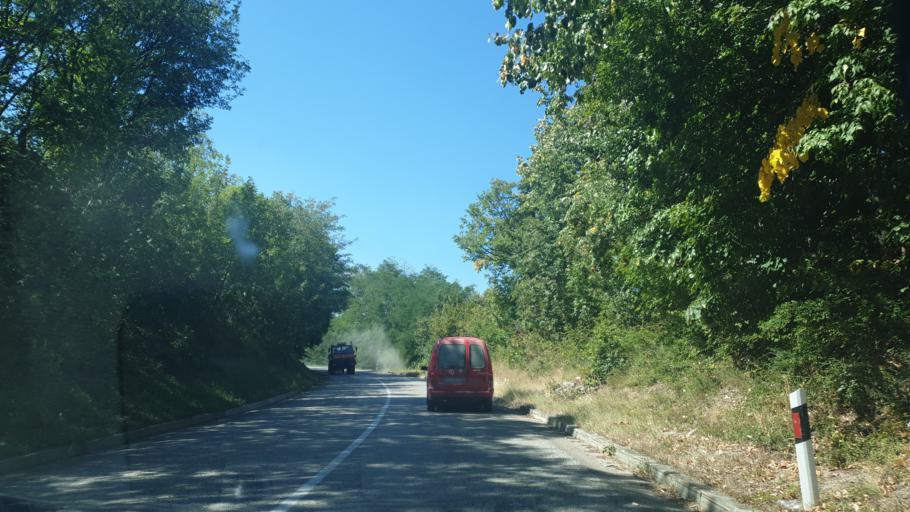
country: RS
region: Central Serbia
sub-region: Kolubarski Okrug
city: Mionica
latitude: 44.1808
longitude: 20.0519
